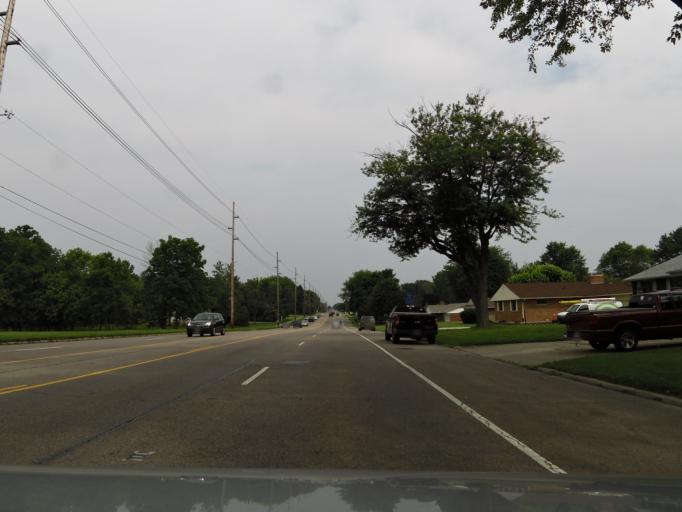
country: US
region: Ohio
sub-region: Greene County
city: Bellbrook
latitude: 39.6718
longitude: -84.1130
